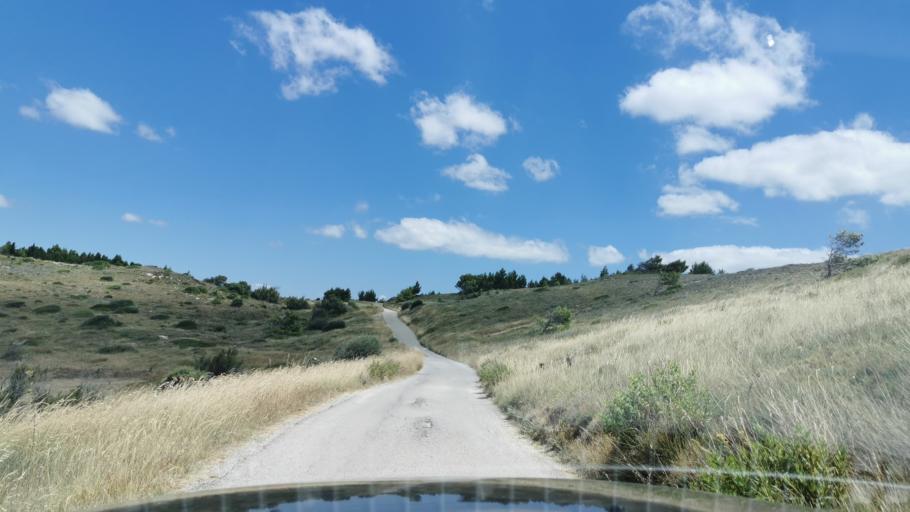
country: FR
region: Languedoc-Roussillon
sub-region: Departement de l'Aude
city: Peyriac-de-Mer
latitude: 43.0881
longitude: 2.9794
